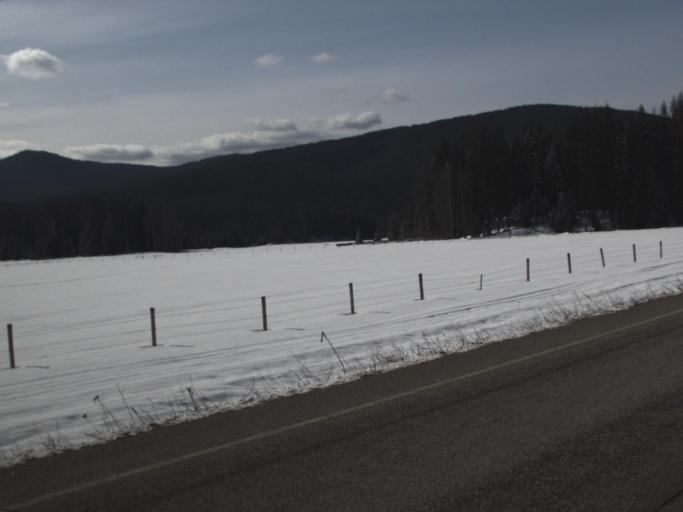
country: US
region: Washington
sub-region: Stevens County
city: Colville
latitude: 48.6686
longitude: -117.4736
